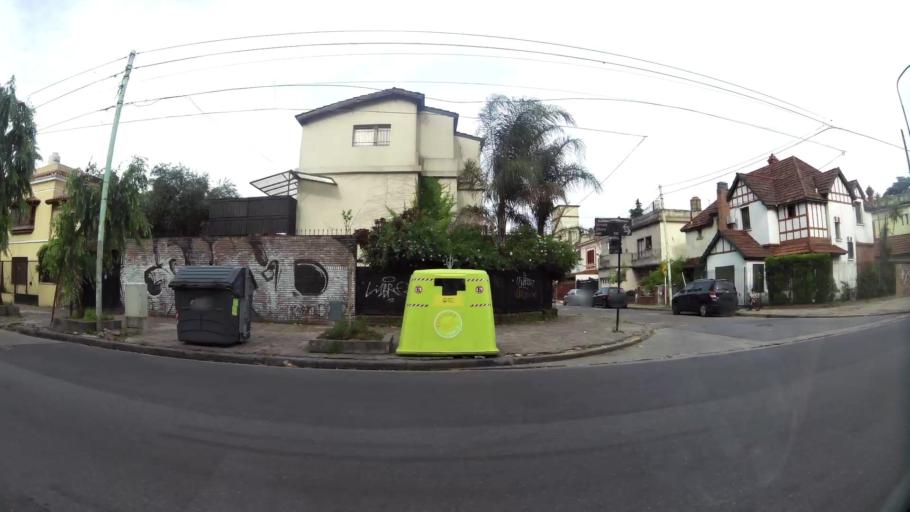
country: AR
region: Buenos Aires F.D.
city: Villa Santa Rita
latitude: -34.6413
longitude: -58.4858
